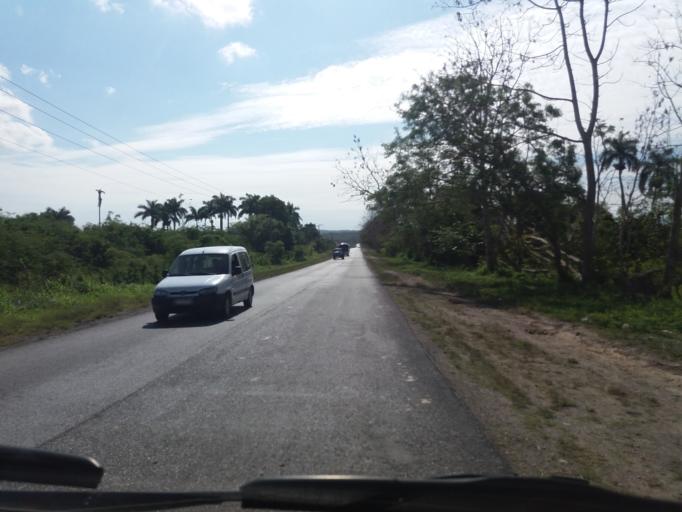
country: CU
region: Cienfuegos
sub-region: Municipio de Cienfuegos
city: Cienfuegos
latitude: 22.1657
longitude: -80.3841
